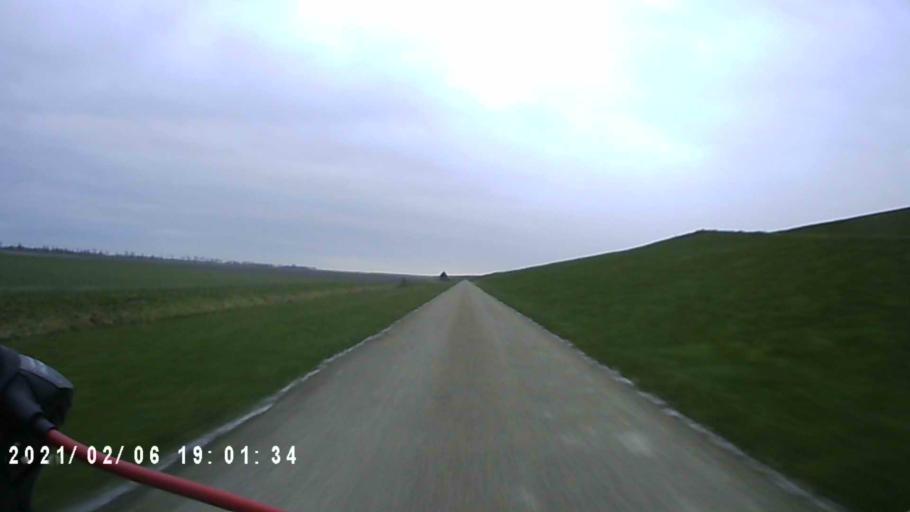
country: NL
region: Groningen
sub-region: Gemeente Winsum
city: Winsum
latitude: 53.4237
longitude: 6.4905
